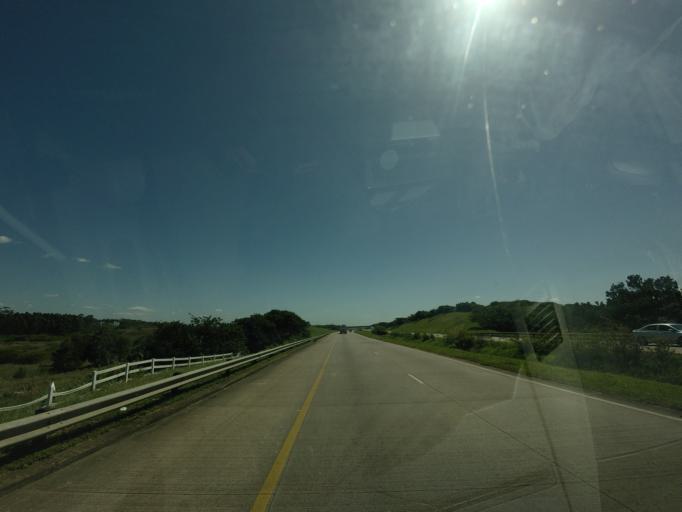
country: ZA
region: KwaZulu-Natal
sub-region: iLembe District Municipality
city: Ballitoville
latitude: -29.4667
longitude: 31.2386
